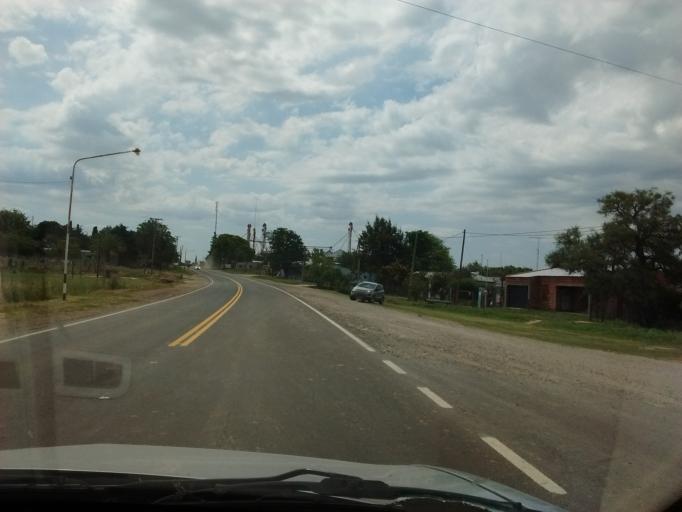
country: AR
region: Entre Rios
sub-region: Departamento de Victoria
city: Victoria
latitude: -32.7828
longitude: -59.9052
